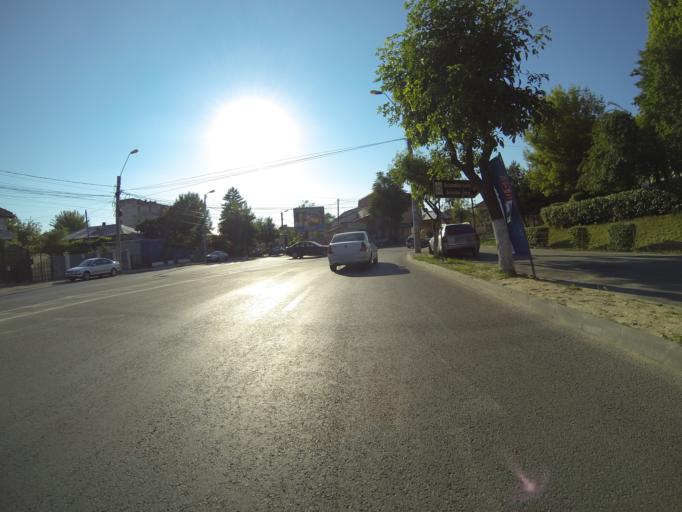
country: RO
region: Dolj
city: Craiova
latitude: 44.3052
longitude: 23.8111
